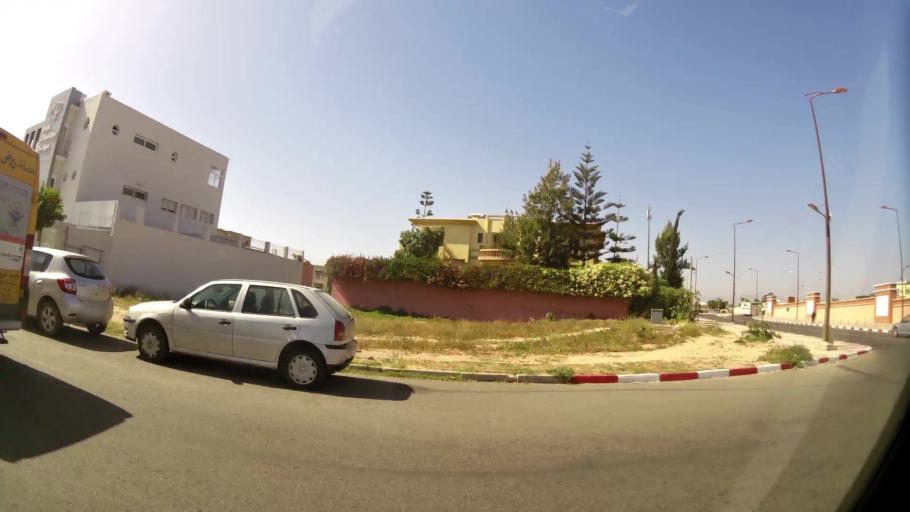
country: MA
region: Souss-Massa-Draa
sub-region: Inezgane-Ait Mellou
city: Inezgane
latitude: 30.3636
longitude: -9.5454
